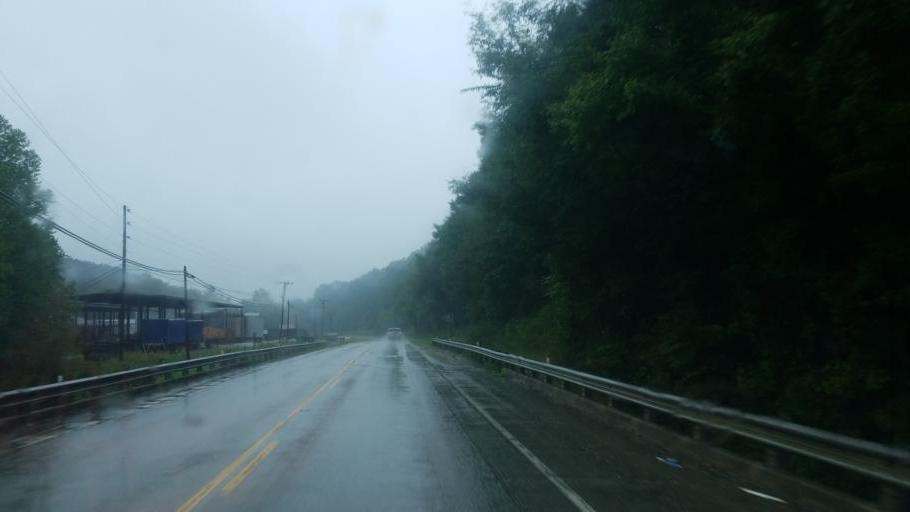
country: US
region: Kentucky
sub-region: Rowan County
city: Morehead
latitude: 38.2227
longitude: -83.4881
